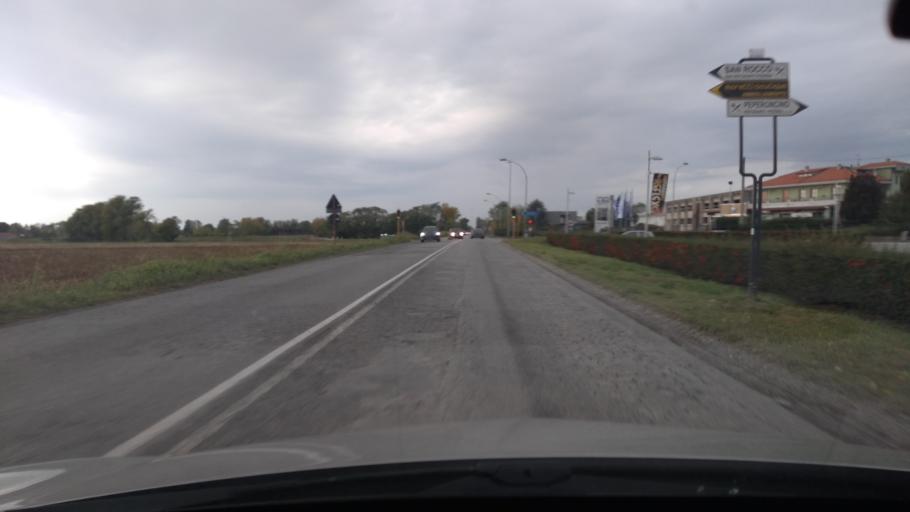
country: IT
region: Lombardy
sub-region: Provincia di Bergamo
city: Urgnano
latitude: 45.5917
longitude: 9.6879
